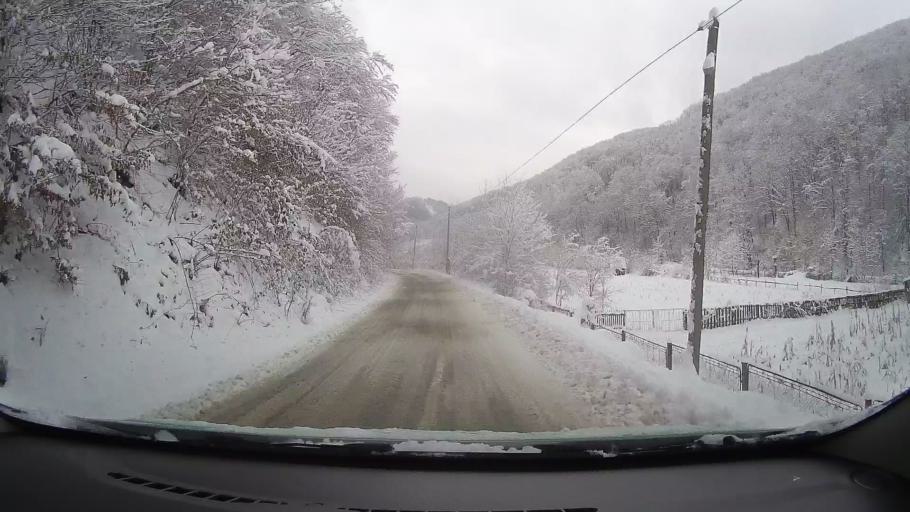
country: RO
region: Alba
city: Pianu de Sus
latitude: 45.8653
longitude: 23.4977
